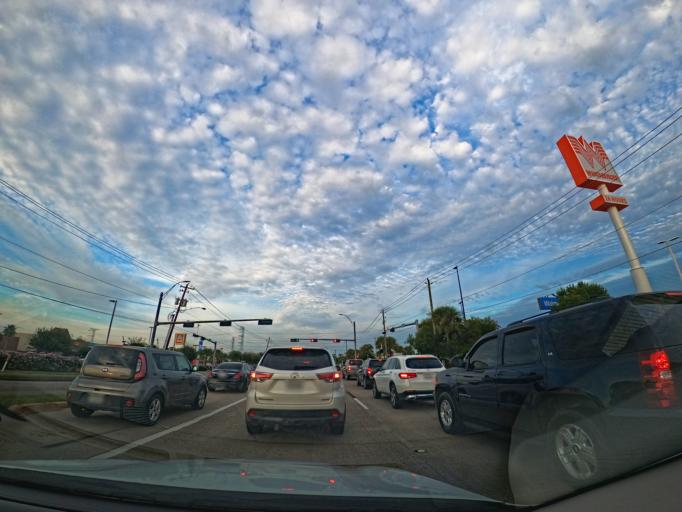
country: US
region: Texas
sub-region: Galveston County
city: Kemah
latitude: 29.5360
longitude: -95.0210
